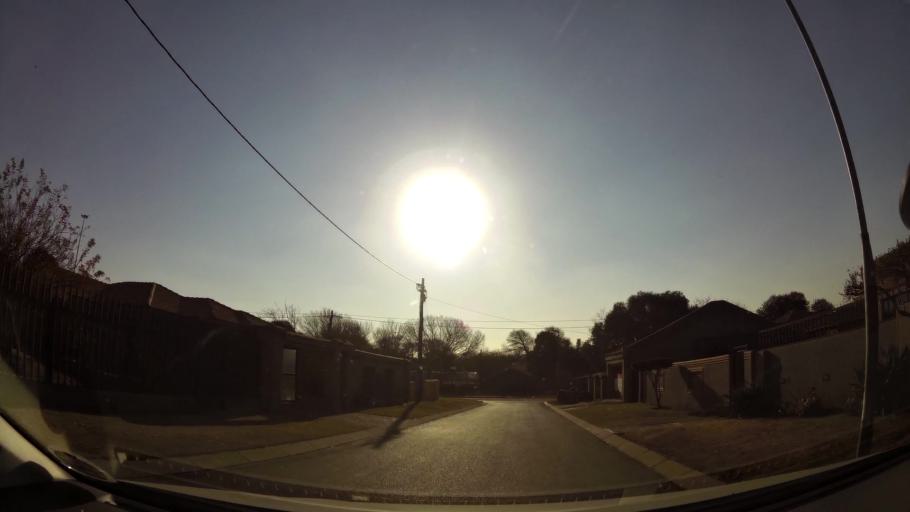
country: ZA
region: Gauteng
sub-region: City of Johannesburg Metropolitan Municipality
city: Soweto
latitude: -26.2639
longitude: 27.8713
